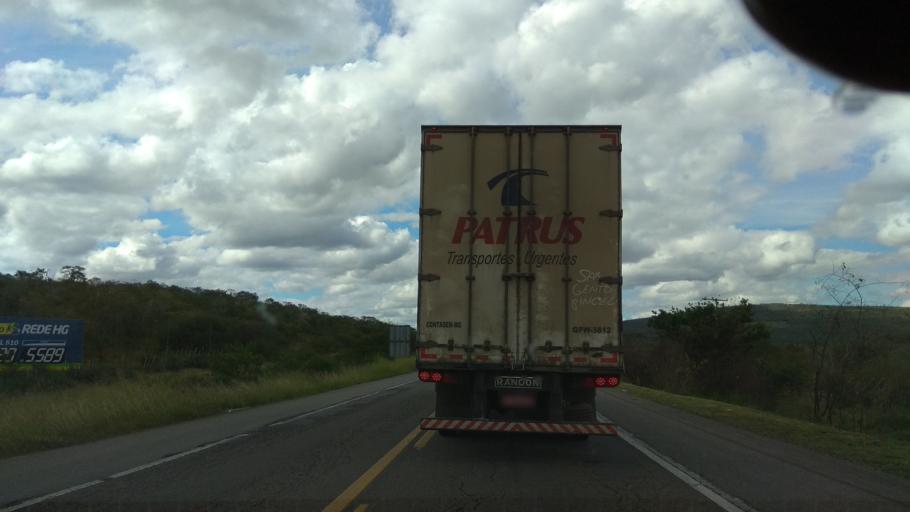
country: BR
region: Bahia
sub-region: Santa Ines
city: Santa Ines
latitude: -12.9939
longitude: -39.9518
